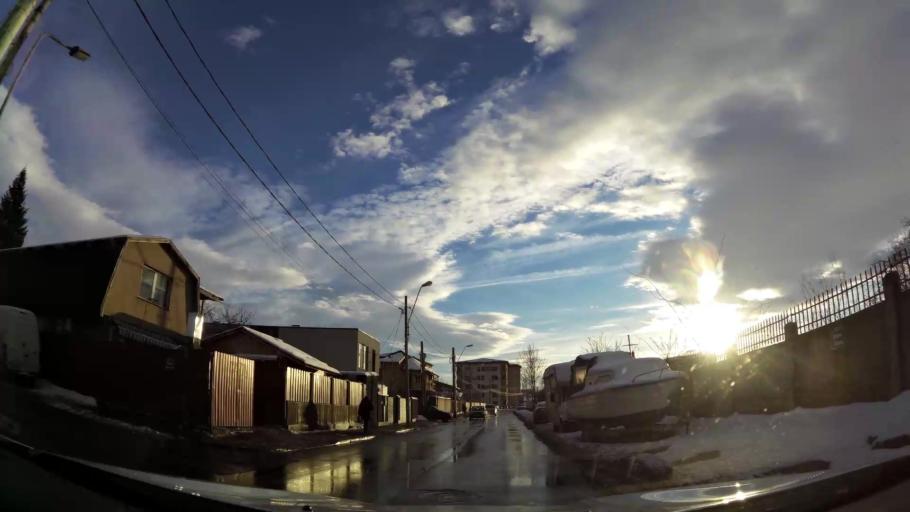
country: RO
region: Ilfov
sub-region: Comuna Popesti-Leordeni
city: Popesti-Leordeni
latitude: 44.3748
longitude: 26.1313
